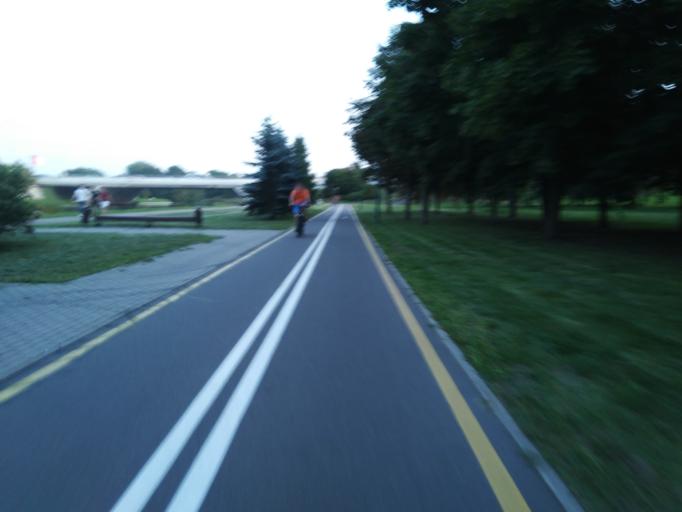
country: BY
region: Minsk
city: Minsk
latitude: 53.9311
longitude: 27.5288
